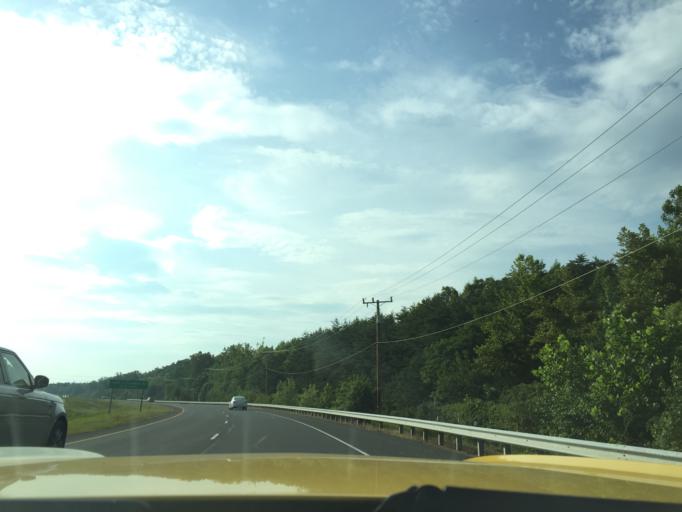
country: US
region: Virginia
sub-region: Fairfax County
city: Fort Belvoir
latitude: 38.7166
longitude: -77.1648
